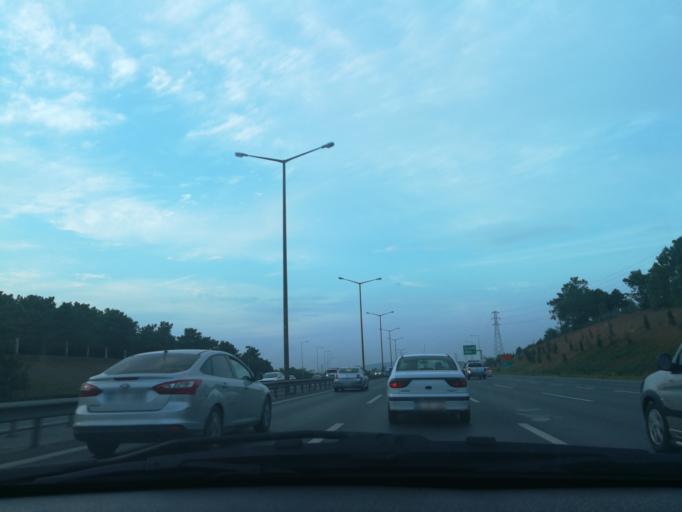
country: TR
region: Istanbul
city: Umraniye
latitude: 41.0409
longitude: 29.1213
